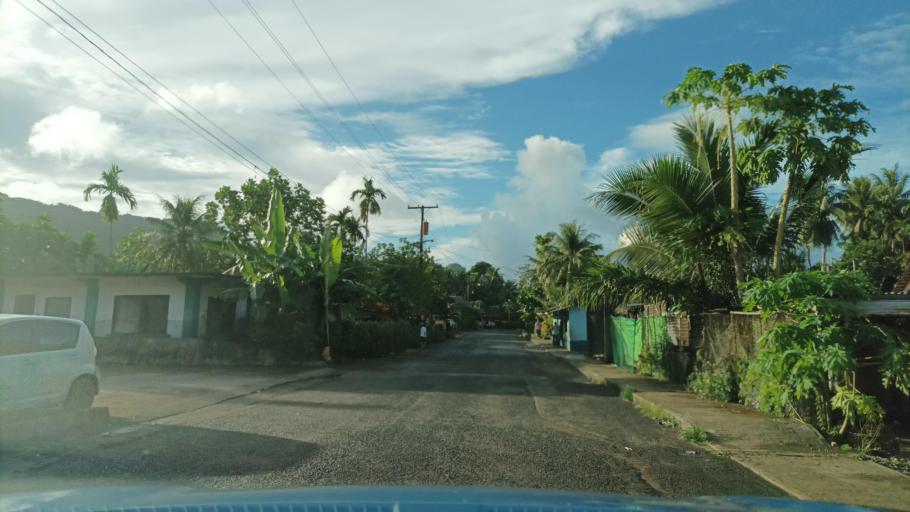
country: FM
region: Pohnpei
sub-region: Kolonia Municipality
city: Kolonia Town
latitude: 6.9623
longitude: 158.2052
